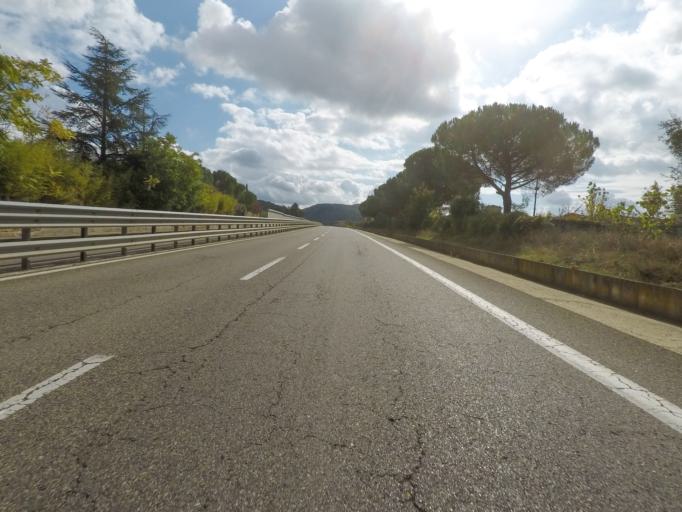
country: IT
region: Tuscany
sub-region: Provincia di Siena
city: Rapolano Terme
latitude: 43.2970
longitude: 11.6023
